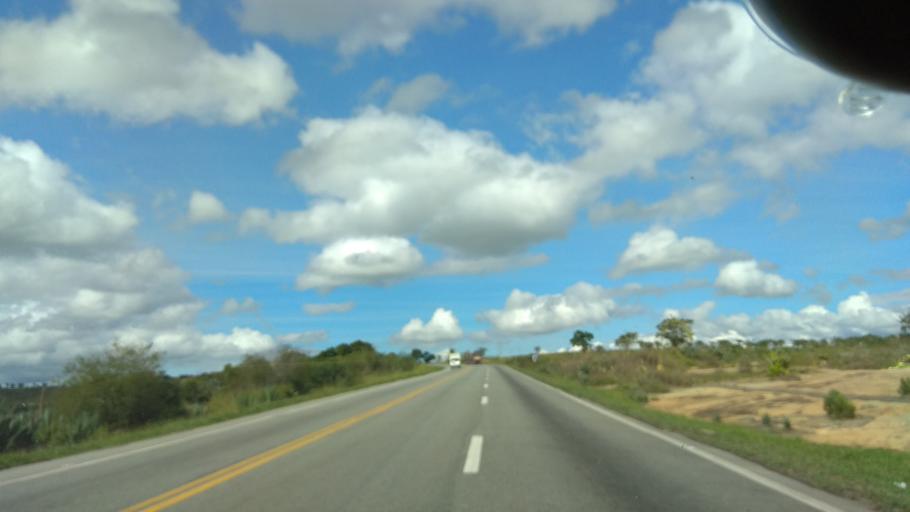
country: BR
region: Bahia
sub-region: Santa Ines
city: Santa Ines
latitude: -13.1062
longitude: -39.9795
